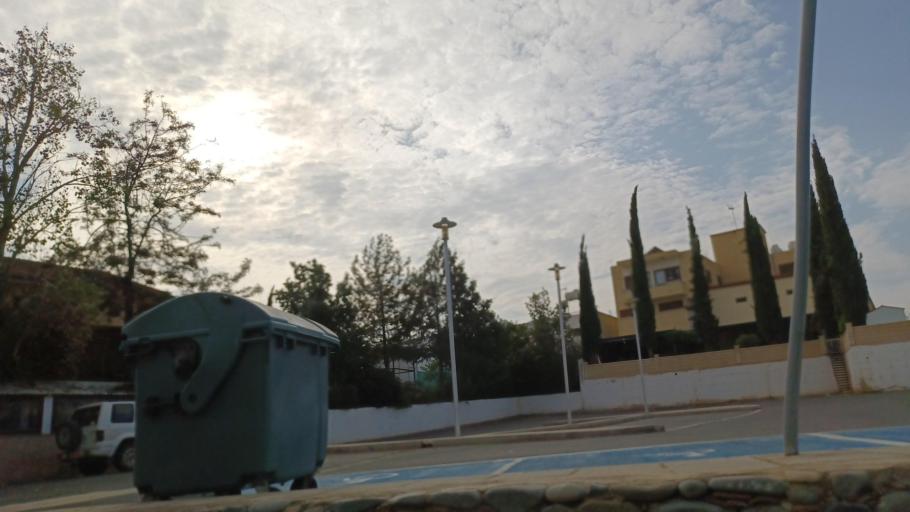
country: CY
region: Lefkosia
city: Peristerona
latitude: 35.1309
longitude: 33.0806
